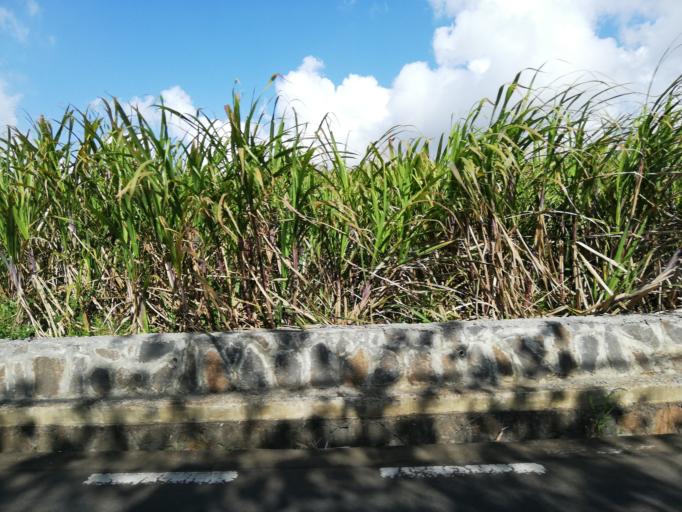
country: MU
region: Pamplemousses
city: Creve Coeur
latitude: -20.2034
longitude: 57.5700
